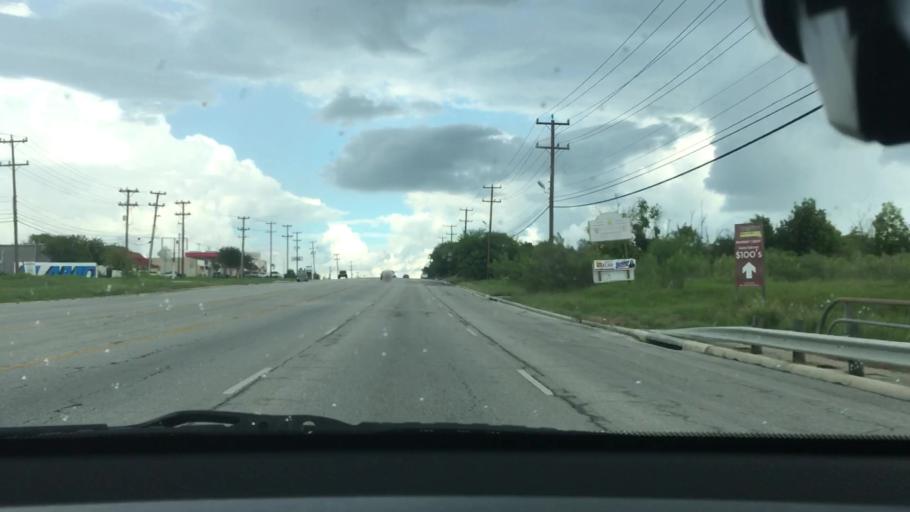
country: US
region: Texas
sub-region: Bexar County
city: Windcrest
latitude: 29.5029
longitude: -98.3659
